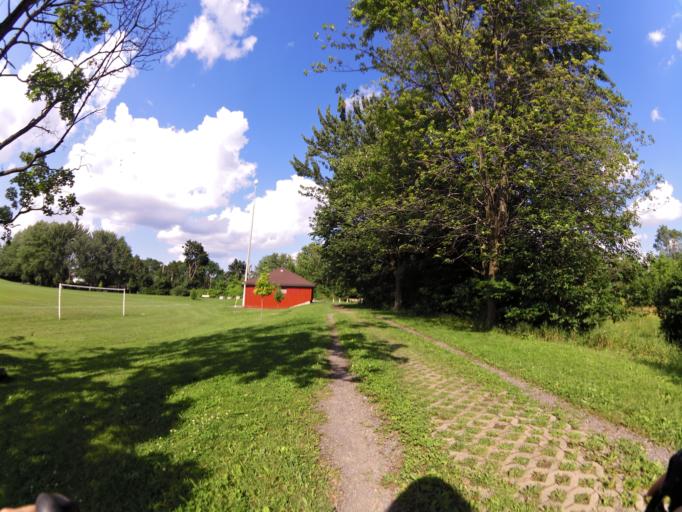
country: CA
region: Ontario
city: Ottawa
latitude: 45.3871
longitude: -75.6877
